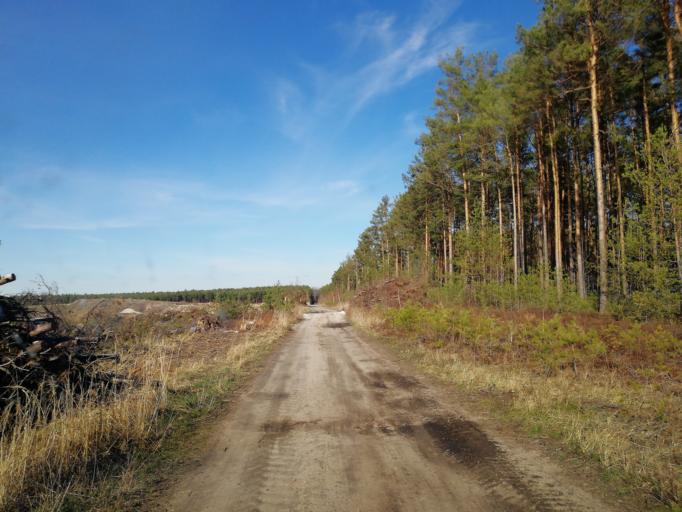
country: DE
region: Brandenburg
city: Ruckersdorf
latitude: 51.5714
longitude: 13.5953
